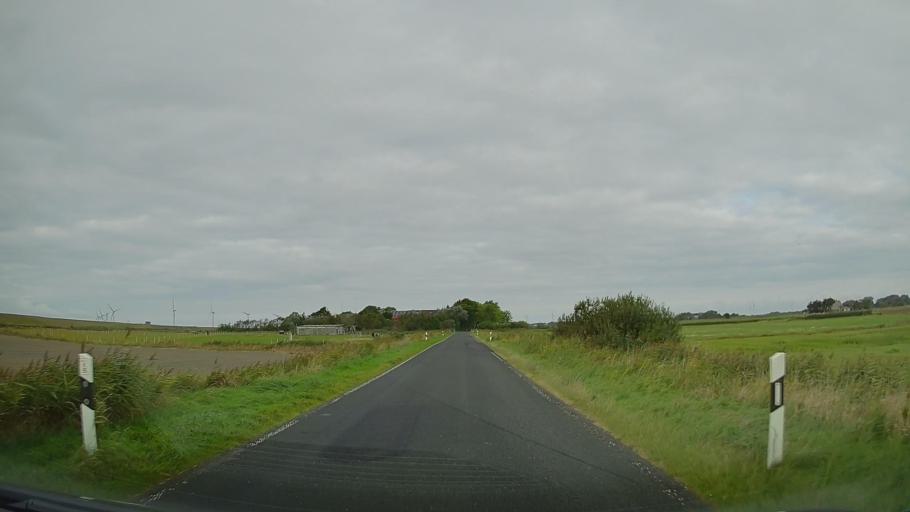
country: DE
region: Schleswig-Holstein
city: Emmelsbull-Horsbull
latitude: 54.8144
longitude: 8.6523
